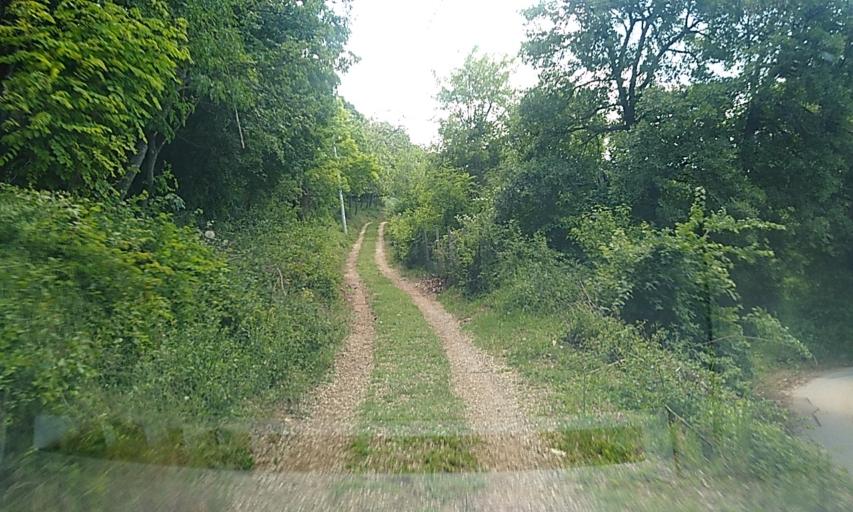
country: RS
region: Central Serbia
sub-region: Nisavski Okrug
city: Niska Banja
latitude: 43.3696
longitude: 21.9950
